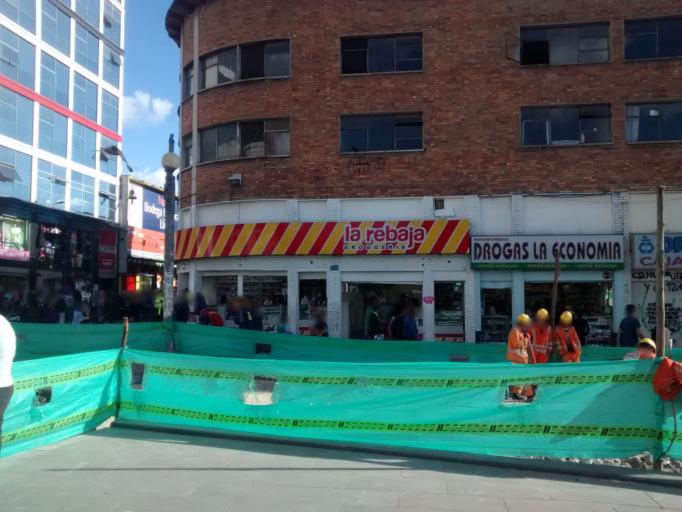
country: CO
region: Bogota D.C.
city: Bogota
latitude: 4.6015
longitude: -74.0783
